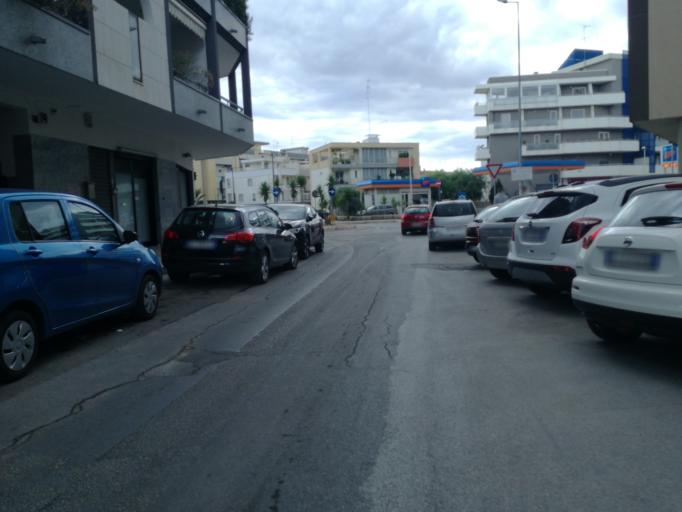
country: IT
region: Apulia
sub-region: Provincia di Bari
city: Triggiano
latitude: 41.0697
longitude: 16.9325
